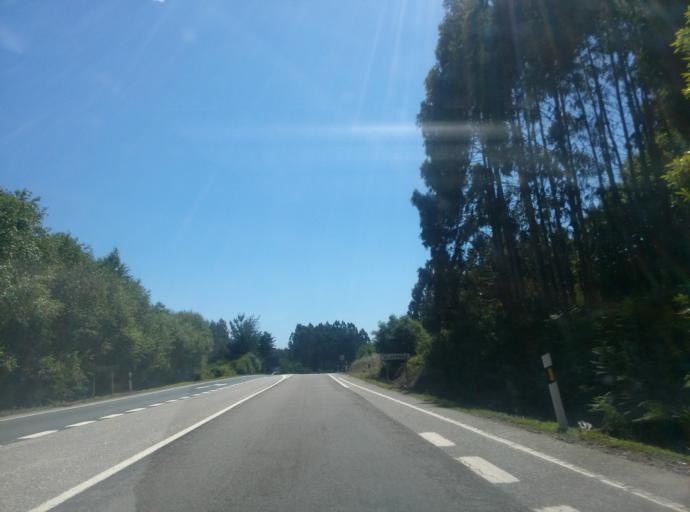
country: ES
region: Galicia
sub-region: Provincia de Lugo
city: Castro de Rei
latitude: 43.1583
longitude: -7.3841
